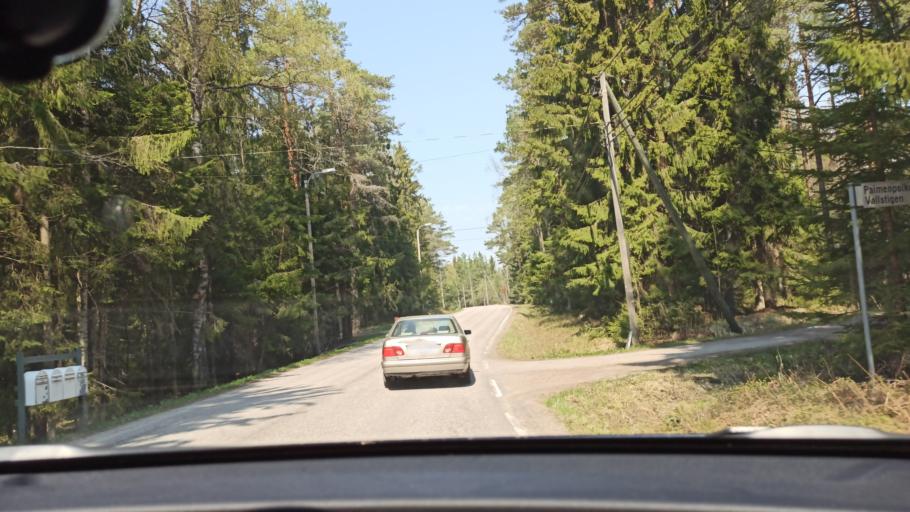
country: FI
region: Uusimaa
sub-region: Helsinki
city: Kirkkonummi
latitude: 60.0965
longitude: 24.5665
